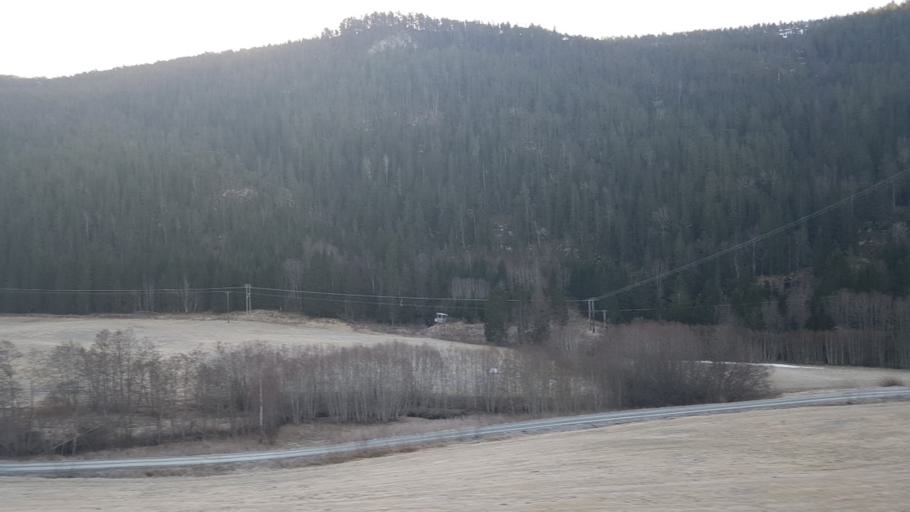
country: NO
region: Nord-Trondelag
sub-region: Stjordal
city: Stjordalshalsen
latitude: 63.5954
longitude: 11.0190
